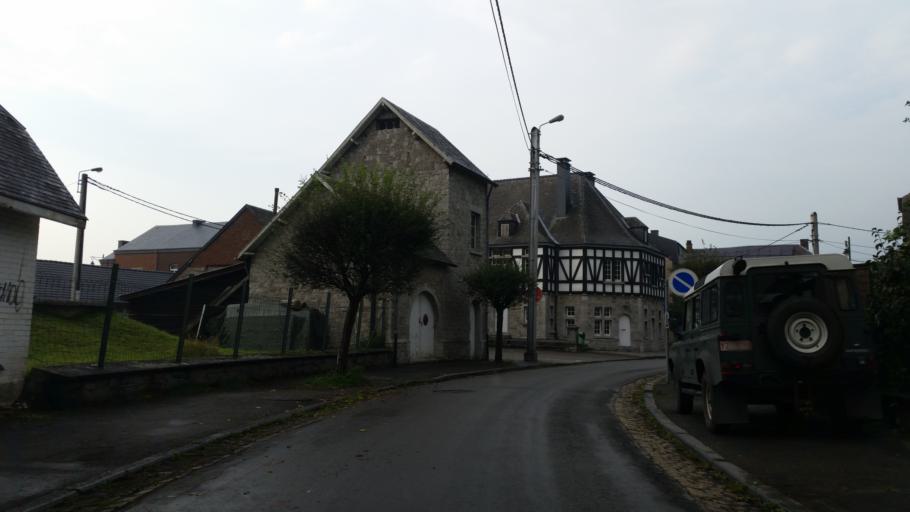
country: BE
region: Wallonia
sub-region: Province de Namur
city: Rochefort
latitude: 50.1255
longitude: 5.1858
